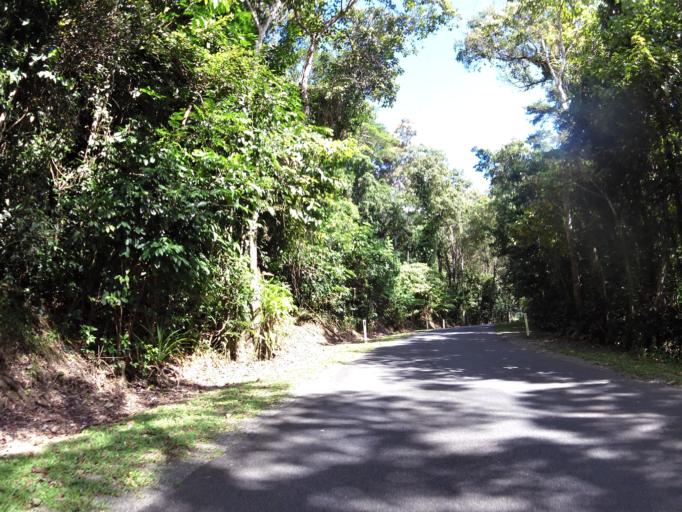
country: AU
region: Queensland
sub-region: Cairns
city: Woree
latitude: -16.9601
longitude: 145.6822
